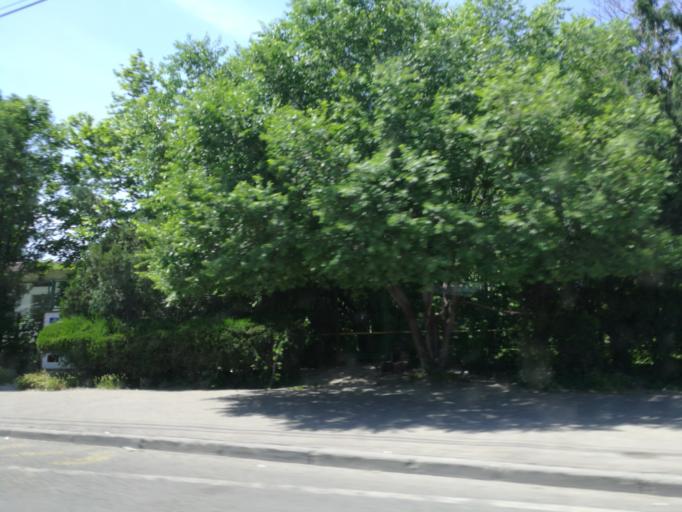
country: RO
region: Constanta
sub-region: Municipiul Constanta
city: Constanta
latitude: 44.2046
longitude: 28.6430
